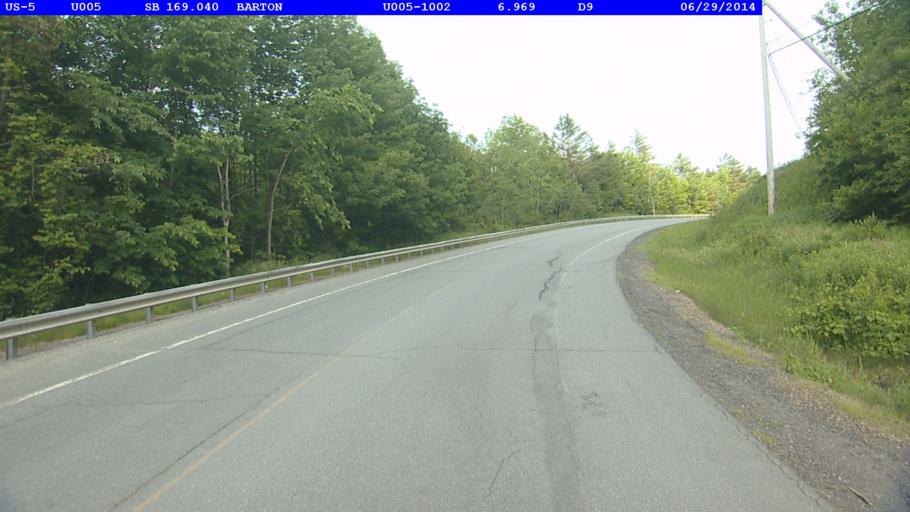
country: US
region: Vermont
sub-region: Orleans County
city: Newport
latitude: 44.7620
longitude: -72.1996
